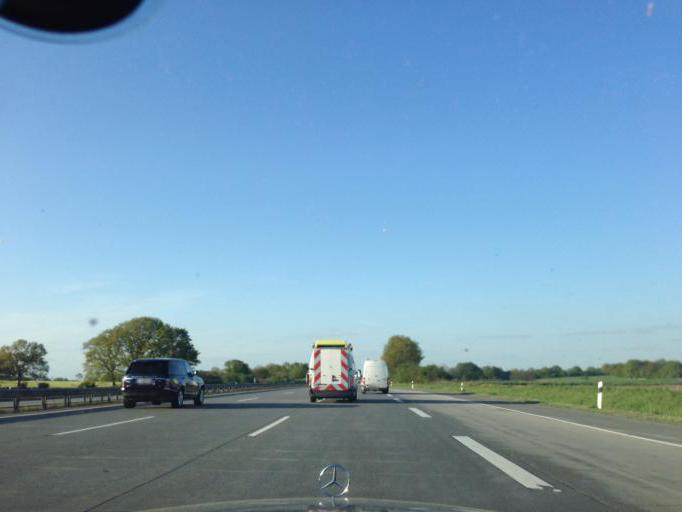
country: DE
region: Schleswig-Holstein
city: Hammoor
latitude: 53.7193
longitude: 10.3395
